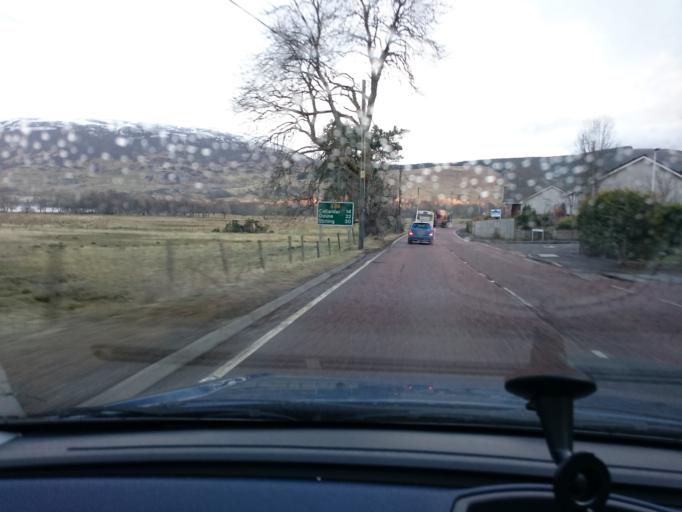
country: GB
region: Scotland
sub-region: Stirling
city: Callander
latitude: 56.3849
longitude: -4.2870
